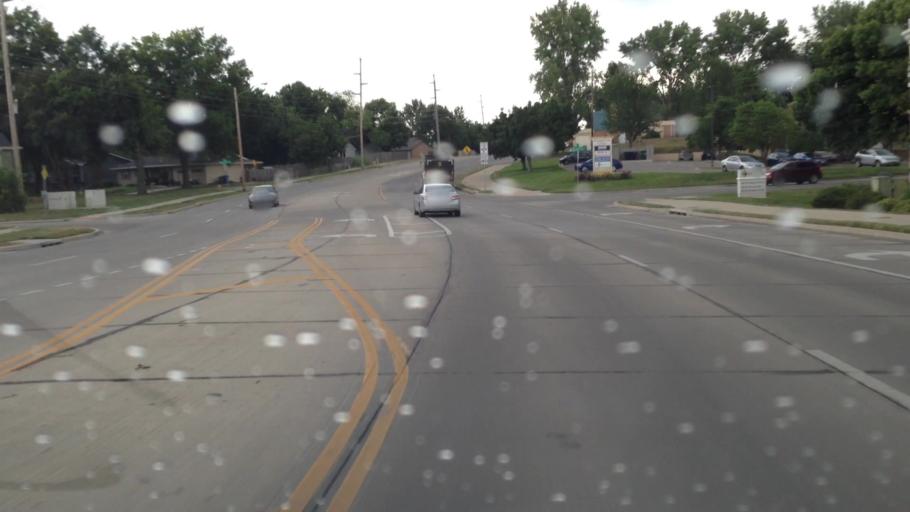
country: US
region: Kansas
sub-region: Douglas County
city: Lawrence
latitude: 38.9421
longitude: -95.2795
